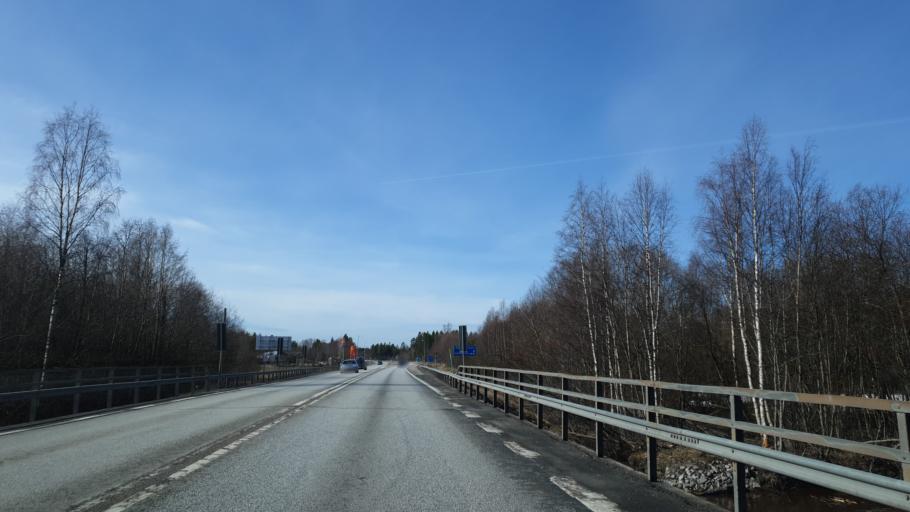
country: SE
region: Vaesterbotten
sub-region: Umea Kommun
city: Hoernefors
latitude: 63.6398
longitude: 19.9176
